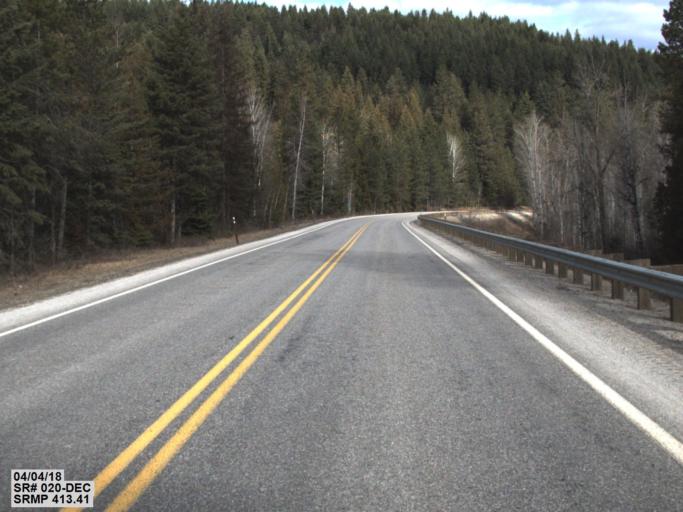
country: US
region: Washington
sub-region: Pend Oreille County
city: Newport
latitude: 48.4165
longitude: -117.3169
